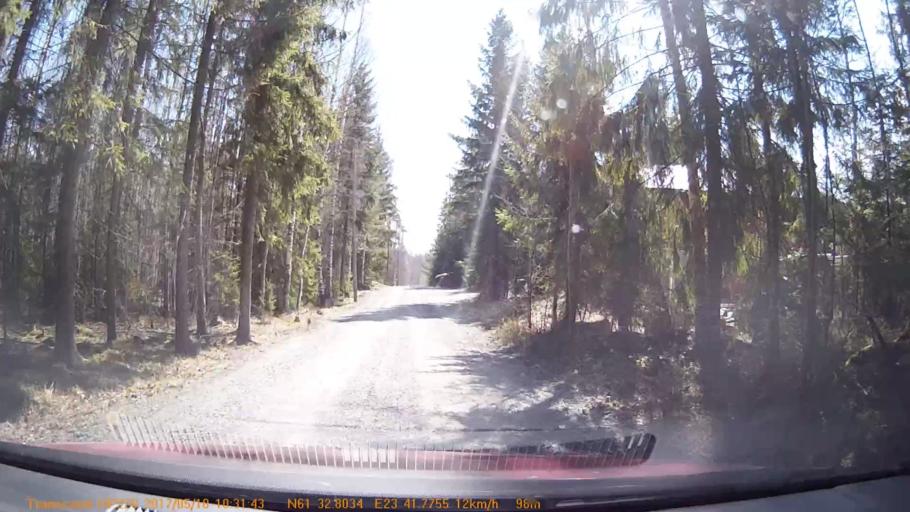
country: FI
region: Pirkanmaa
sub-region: Tampere
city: Yloejaervi
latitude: 61.5468
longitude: 23.6962
